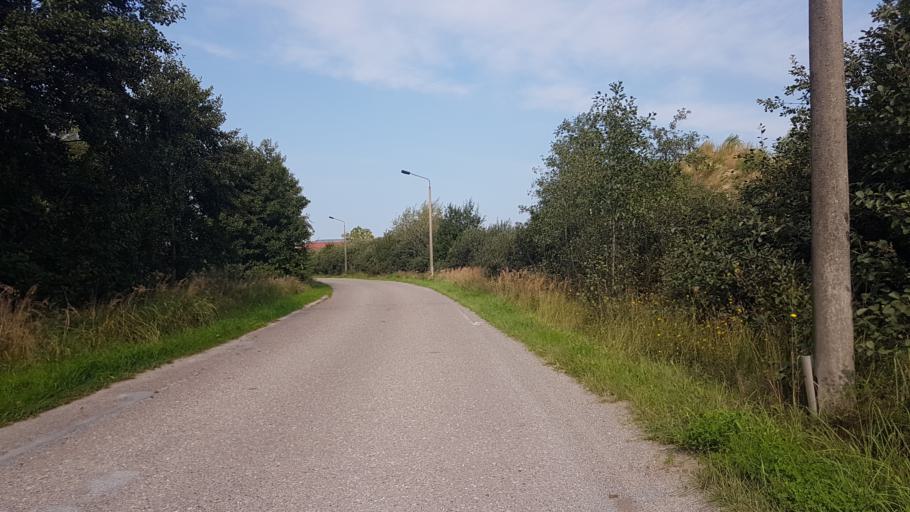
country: DE
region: Mecklenburg-Vorpommern
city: Sagard
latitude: 54.4958
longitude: 13.5524
